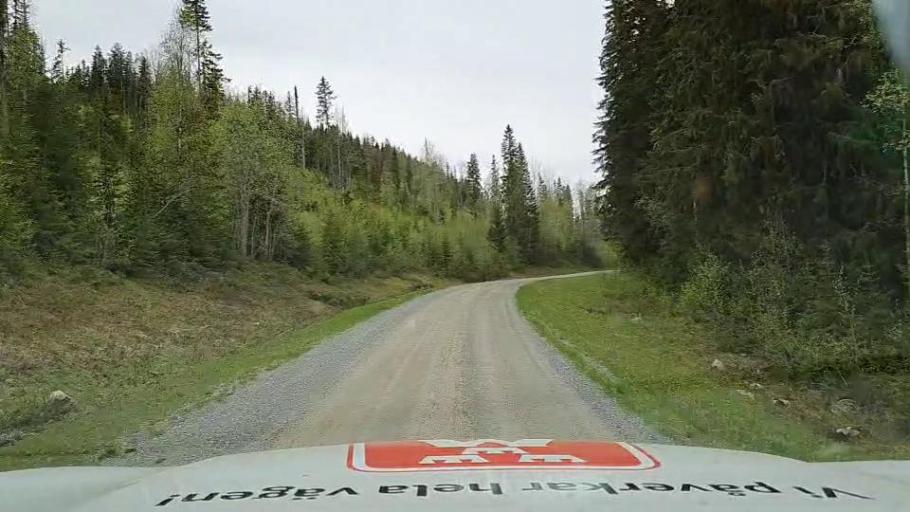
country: SE
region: Jaemtland
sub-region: Bergs Kommun
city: Hoverberg
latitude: 62.5484
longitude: 14.6940
